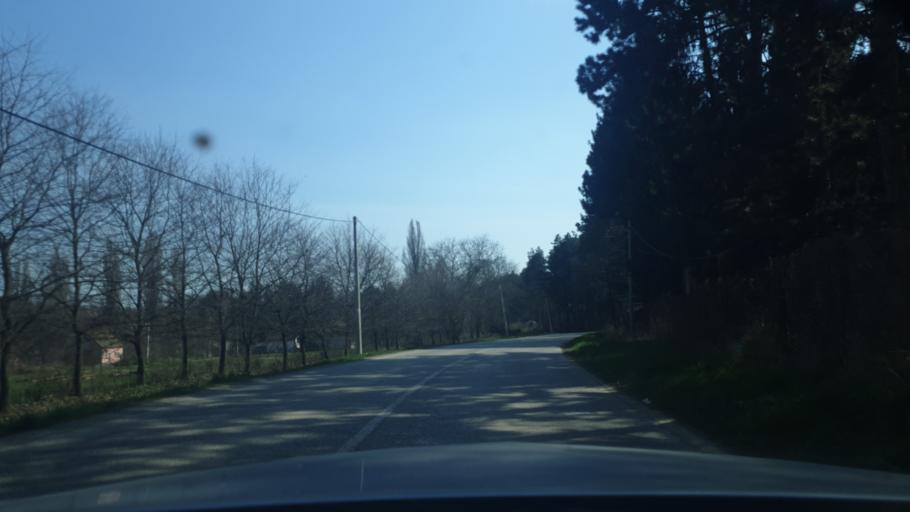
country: RS
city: Vrdnik
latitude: 45.1330
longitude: 19.7822
